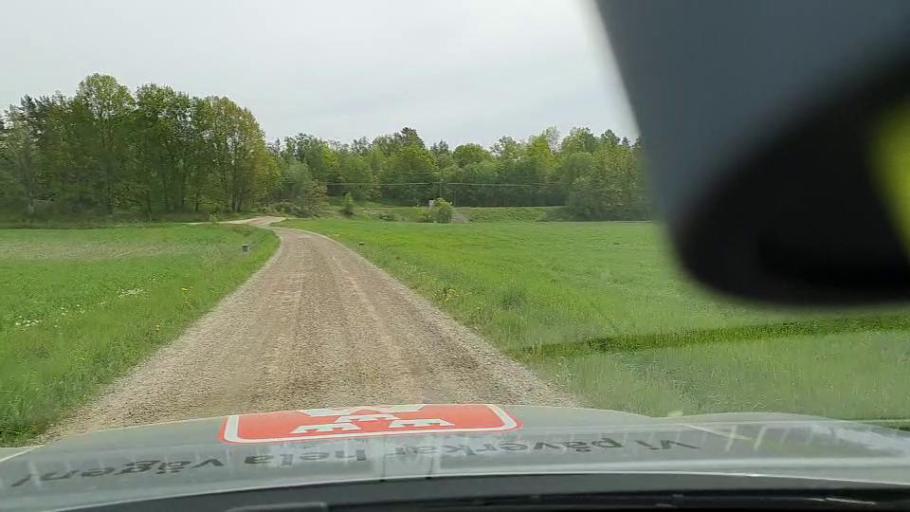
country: SE
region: Soedermanland
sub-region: Flens Kommun
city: Flen
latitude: 59.0411
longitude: 16.5784
